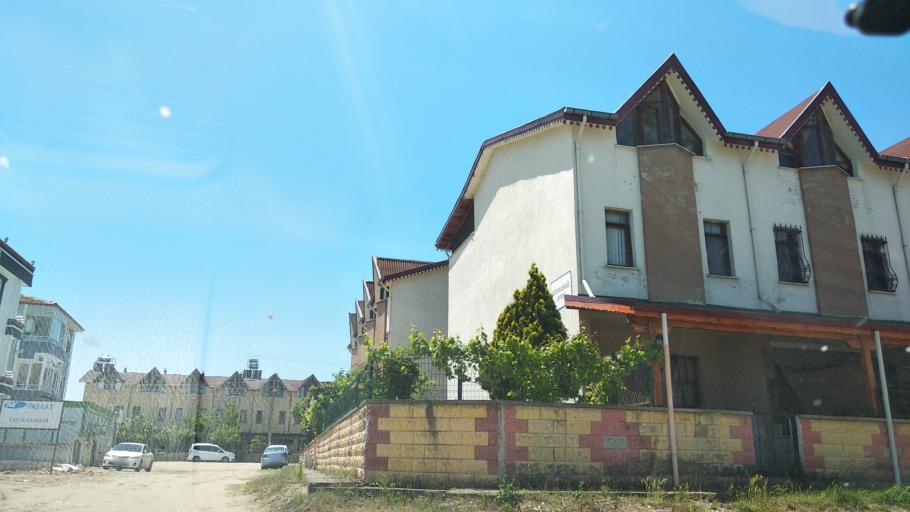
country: TR
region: Sakarya
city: Karasu
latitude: 41.0904
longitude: 30.7362
